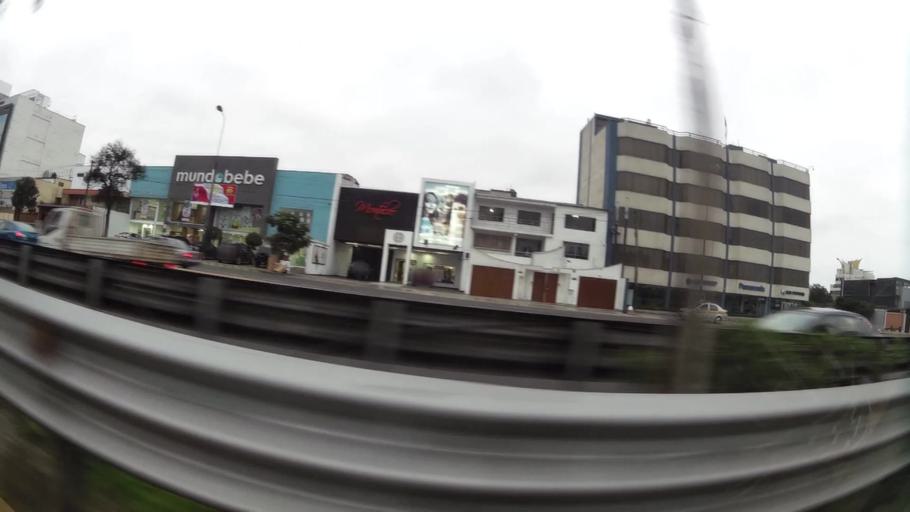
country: PE
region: Lima
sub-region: Lima
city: San Luis
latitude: -12.0893
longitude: -77.0123
